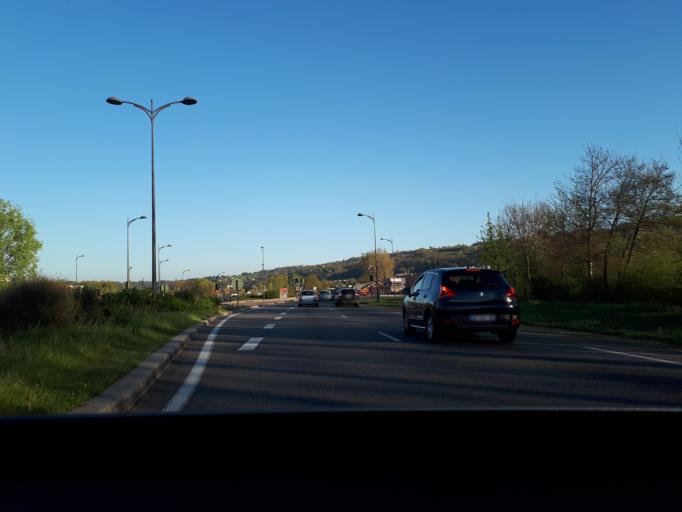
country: FR
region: Rhone-Alpes
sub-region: Departement de l'Isere
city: Domarin
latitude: 45.5972
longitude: 5.2399
